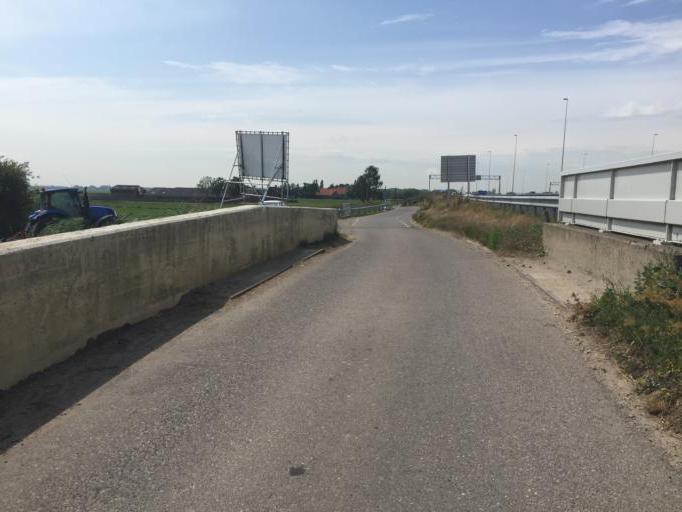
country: NL
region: South Holland
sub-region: Bodegraven-Reeuwijk
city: Bodegraven
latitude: 52.0651
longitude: 4.7843
